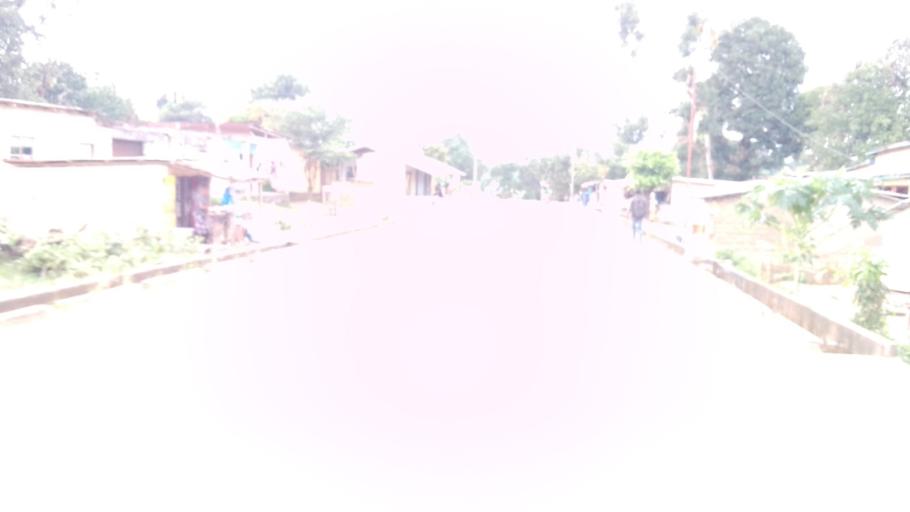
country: SL
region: Eastern Province
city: Koidu
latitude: 8.6564
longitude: -10.9758
